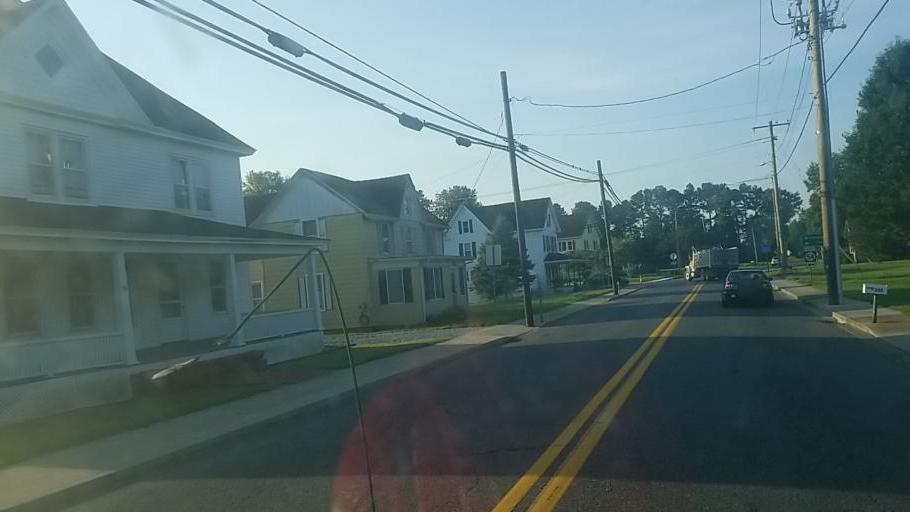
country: US
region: Delaware
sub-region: Sussex County
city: Selbyville
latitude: 38.4572
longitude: -75.2198
